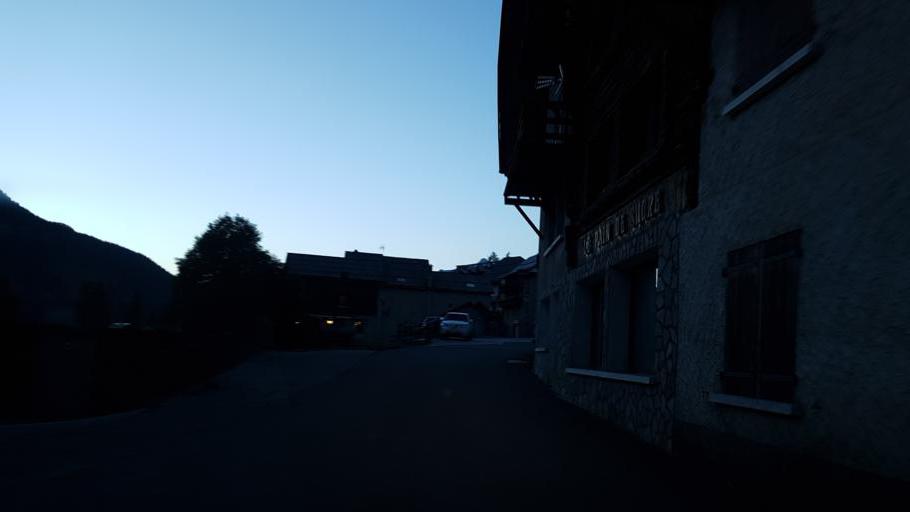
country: FR
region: Provence-Alpes-Cote d'Azur
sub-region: Departement des Hautes-Alpes
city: Guillestre
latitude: 44.7297
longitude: 6.8434
